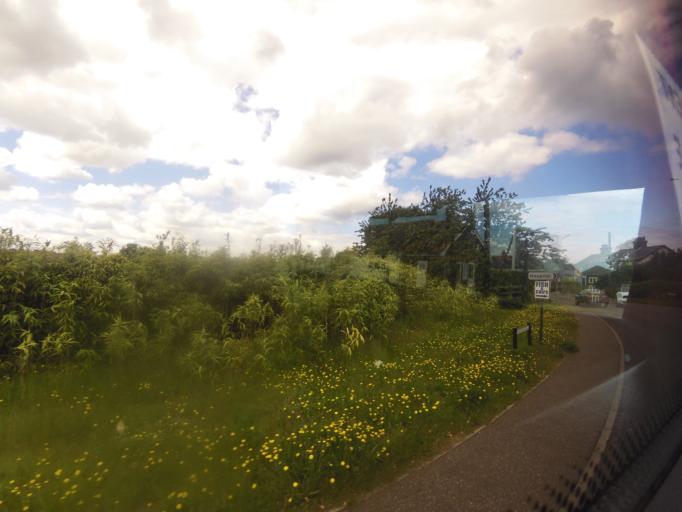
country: GB
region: England
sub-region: Norfolk
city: Cromer
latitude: 52.9180
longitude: 1.3078
